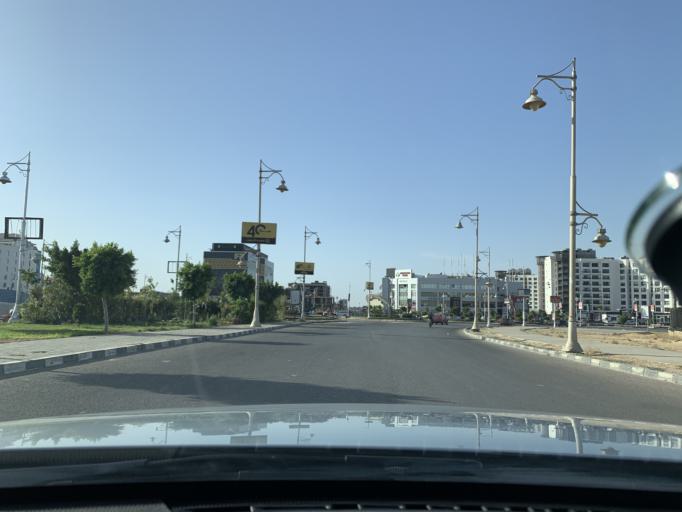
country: EG
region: Muhafazat al Qalyubiyah
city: Al Khankah
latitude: 30.0237
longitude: 31.4957
